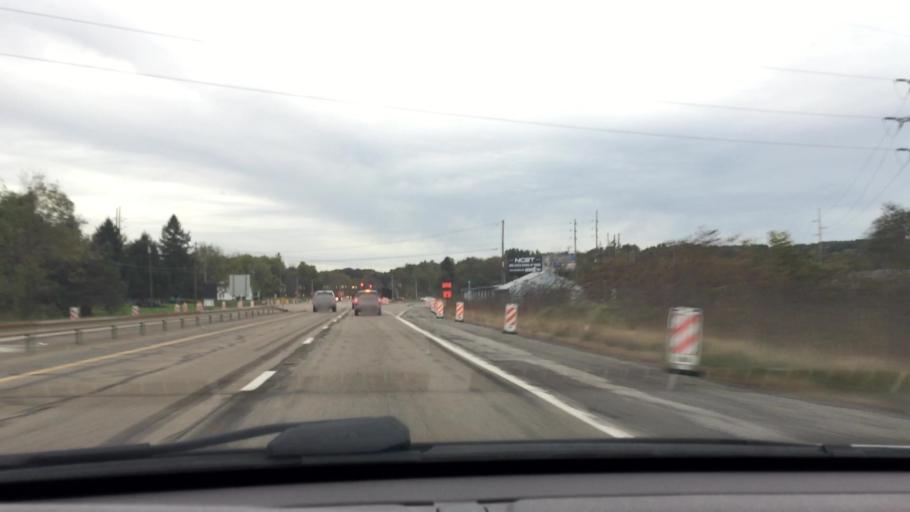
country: US
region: Pennsylvania
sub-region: Lawrence County
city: Oakwood
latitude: 41.0339
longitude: -80.4017
